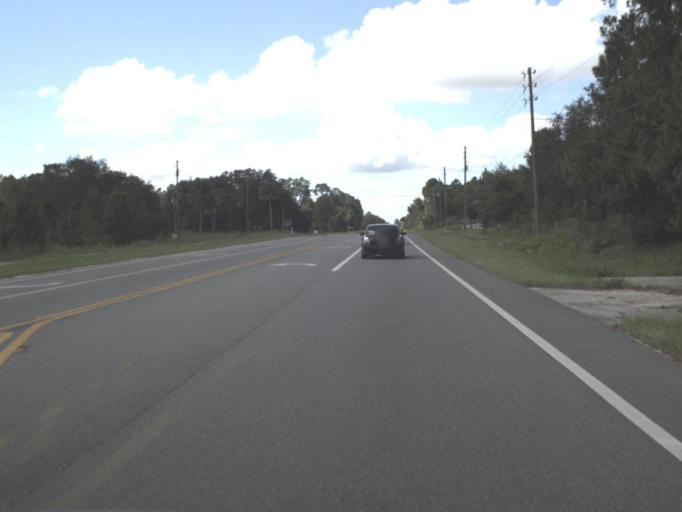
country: US
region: Florida
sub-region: Polk County
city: Loughman
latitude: 28.2149
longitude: -81.5727
